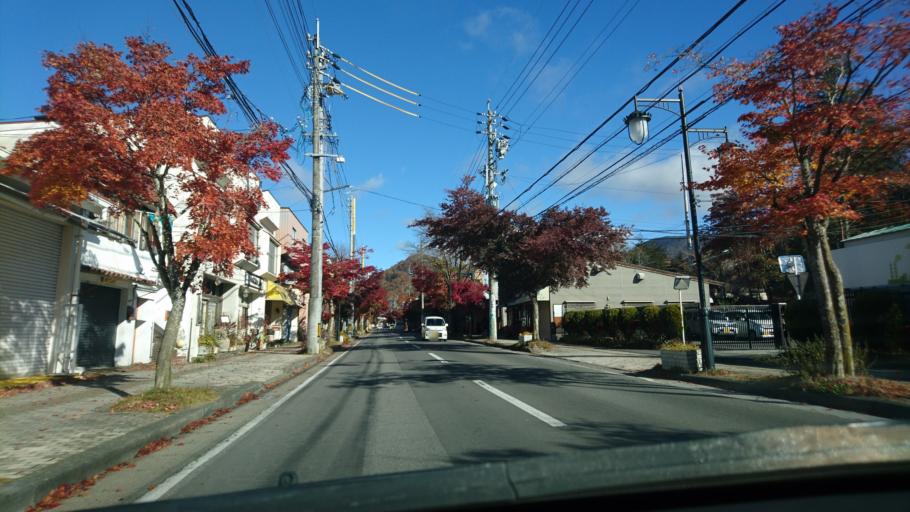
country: JP
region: Nagano
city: Saku
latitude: 36.3541
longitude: 138.6342
